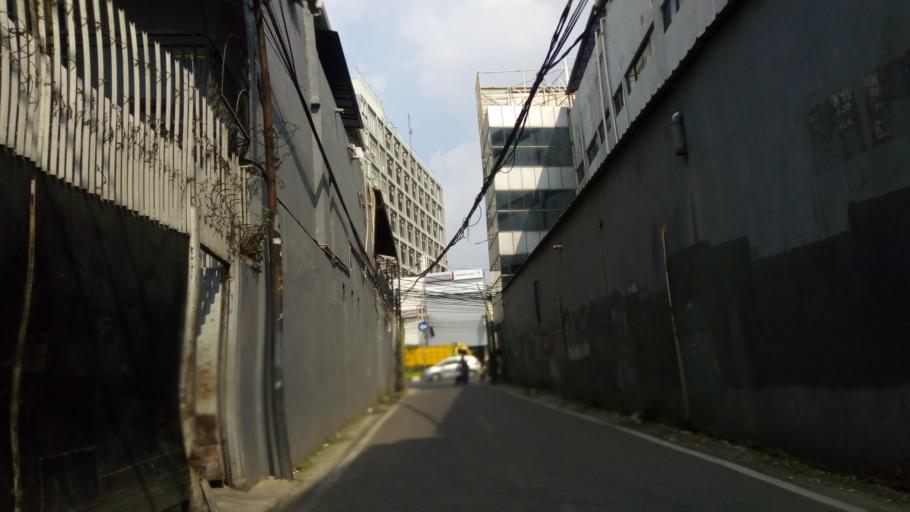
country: ID
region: Jakarta Raya
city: Jakarta
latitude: -6.1612
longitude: 106.8307
